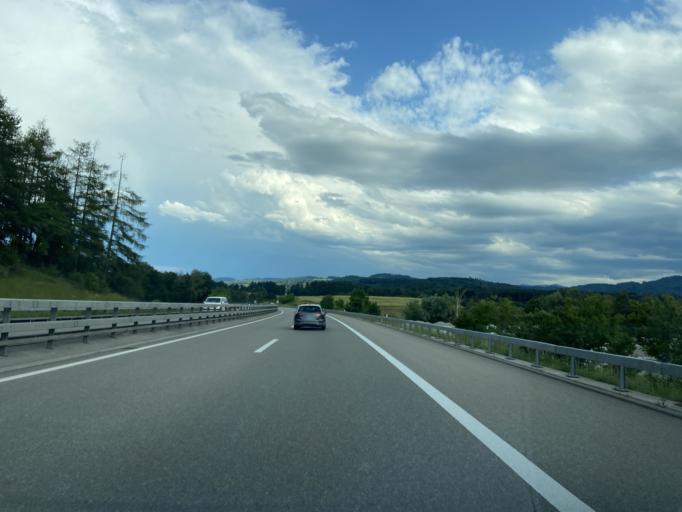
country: CH
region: Thurgau
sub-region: Muenchwilen District
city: Aadorf
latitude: 47.5181
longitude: 8.8987
